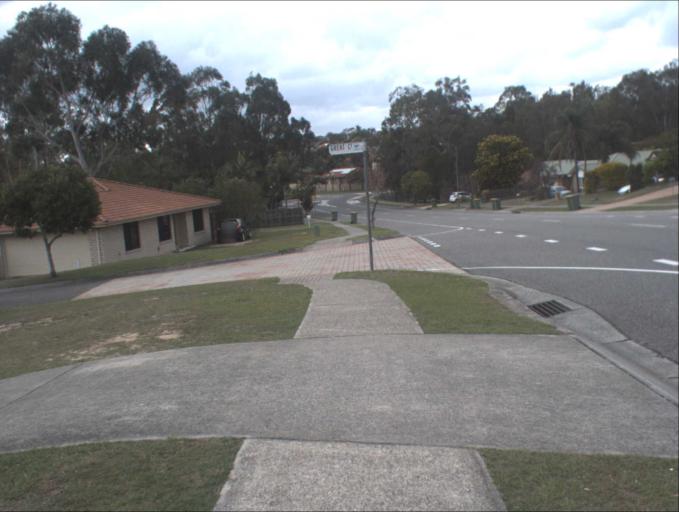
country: AU
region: Queensland
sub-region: Logan
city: Park Ridge South
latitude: -27.6811
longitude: 153.0375
